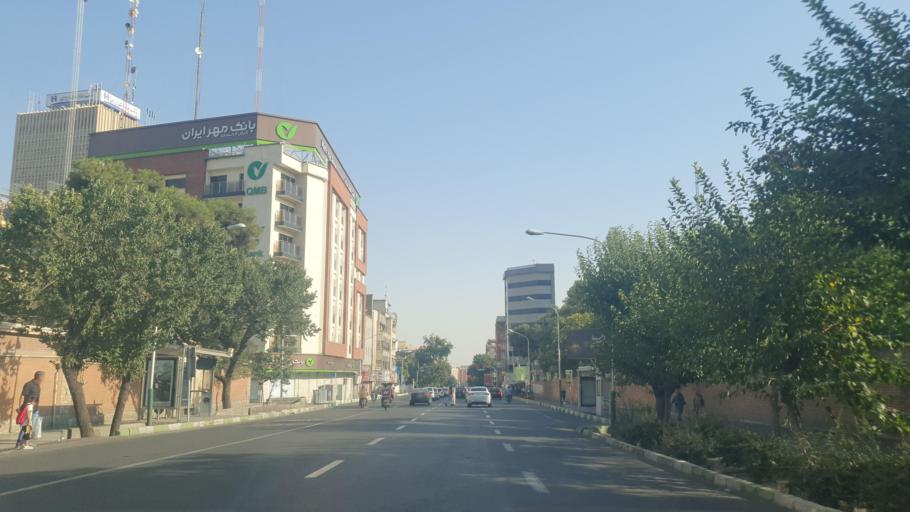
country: IR
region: Tehran
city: Tehran
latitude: 35.7085
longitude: 51.4256
